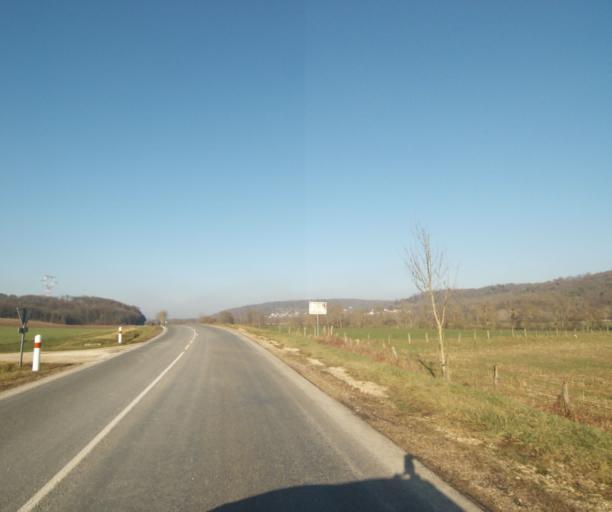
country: FR
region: Champagne-Ardenne
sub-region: Departement de la Haute-Marne
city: Chevillon
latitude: 48.5095
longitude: 5.1129
